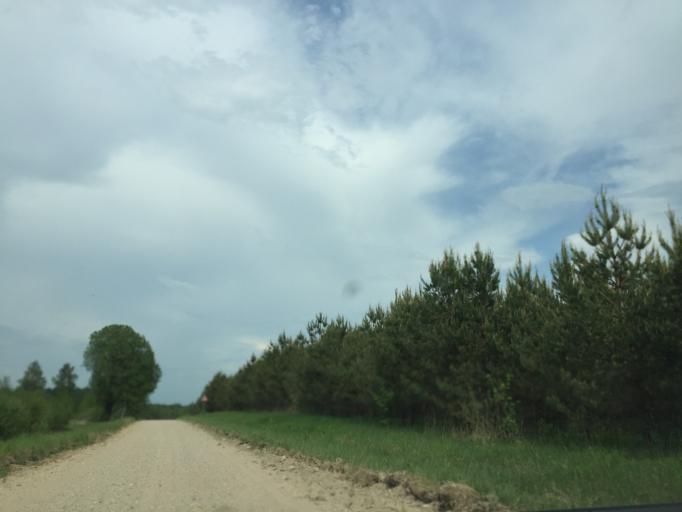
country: LV
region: Livani
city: Livani
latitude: 56.5761
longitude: 26.1723
